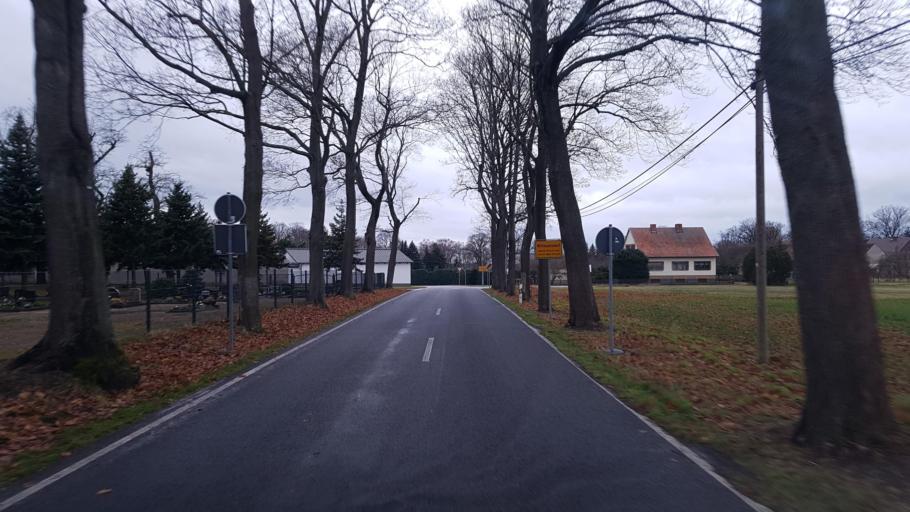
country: DE
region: Brandenburg
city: Tauche
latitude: 52.0754
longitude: 14.0604
